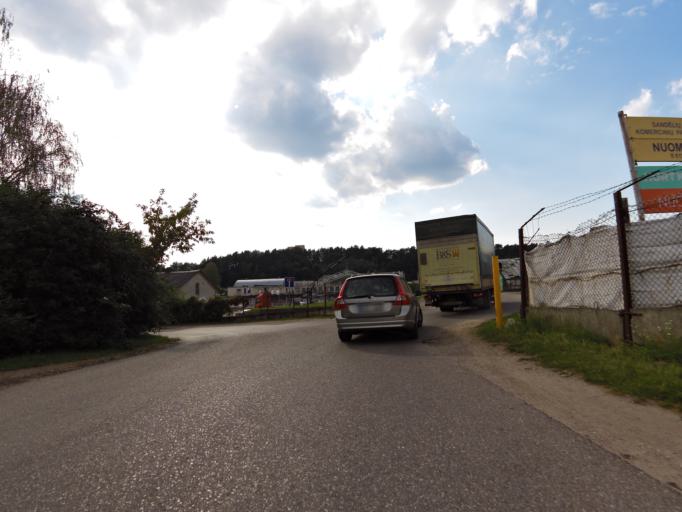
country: LT
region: Vilnius County
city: Lazdynai
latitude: 54.6686
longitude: 25.2252
